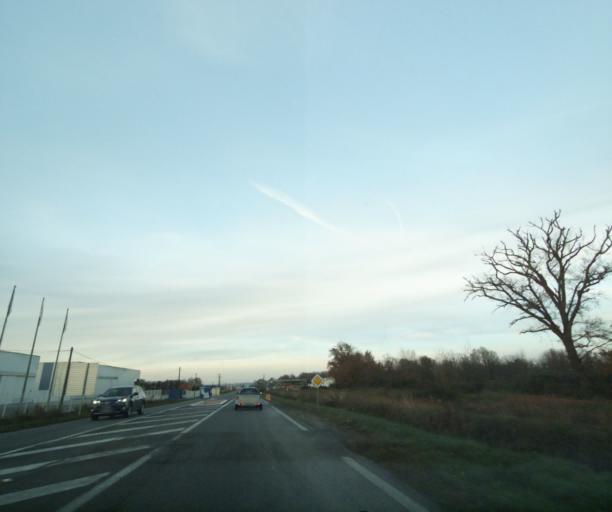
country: FR
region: Aquitaine
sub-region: Departement de la Gironde
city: Langon
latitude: 44.5172
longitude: -0.2396
